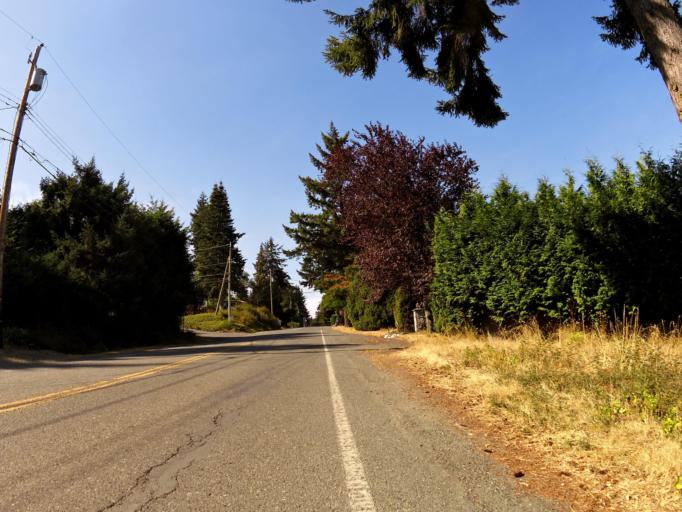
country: CA
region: British Columbia
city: North Saanich
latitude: 48.6373
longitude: -123.5383
